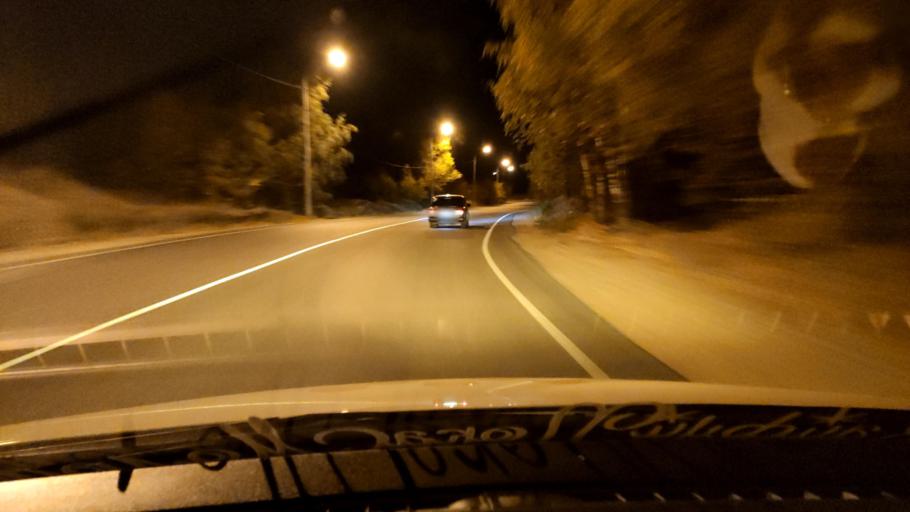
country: RU
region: Voronezj
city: Pridonskoy
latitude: 51.6806
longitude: 39.1147
